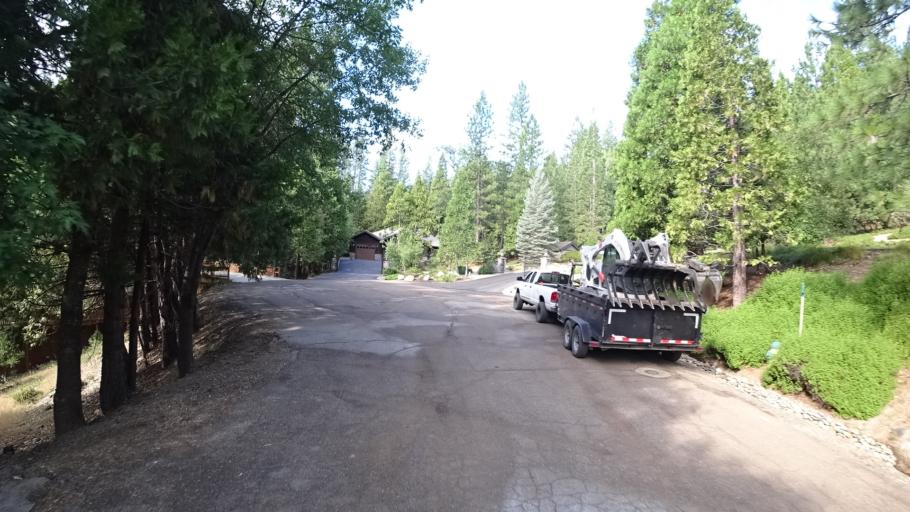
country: US
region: California
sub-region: Calaveras County
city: Arnold
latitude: 38.2546
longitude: -120.3394
